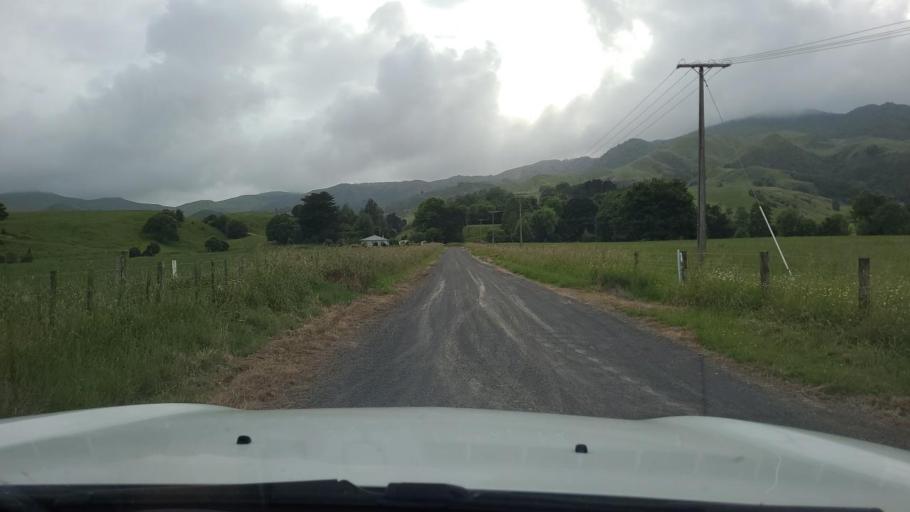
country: NZ
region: Waikato
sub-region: Hauraki District
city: Paeroa
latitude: -37.5107
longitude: 175.6988
